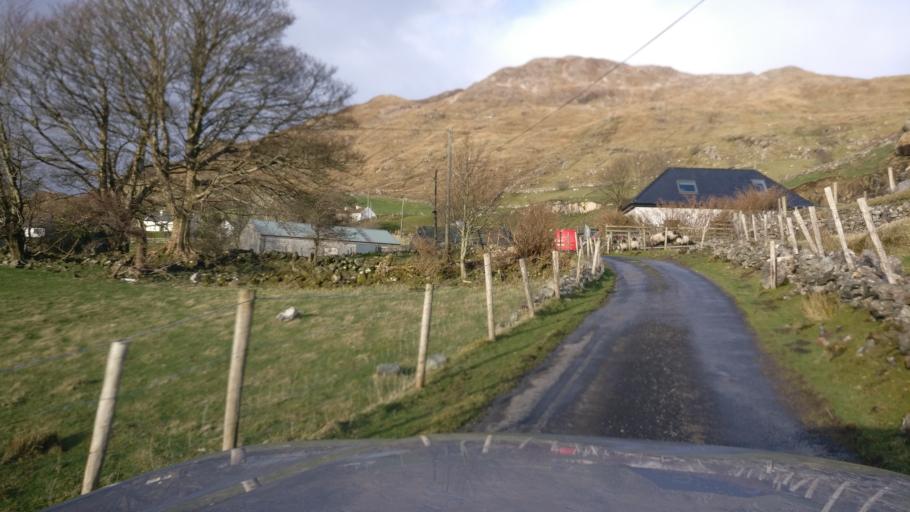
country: IE
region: Connaught
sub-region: County Galway
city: Clifden
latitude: 53.4758
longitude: -9.7260
